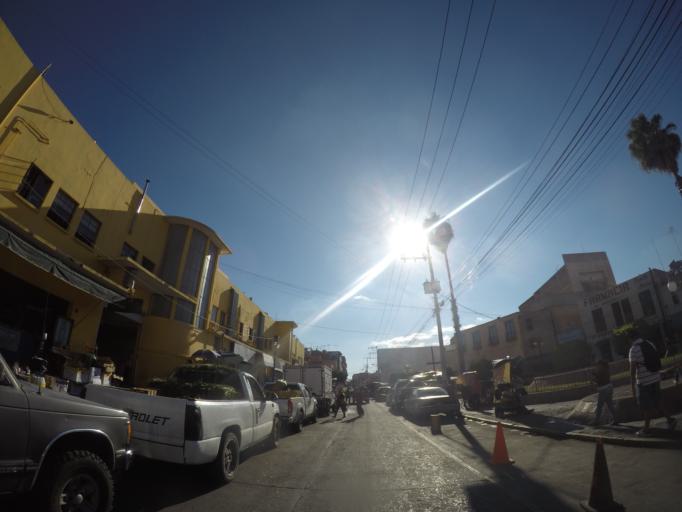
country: MX
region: San Luis Potosi
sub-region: San Luis Potosi
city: San Luis Potosi
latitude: 22.1558
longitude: -100.9762
